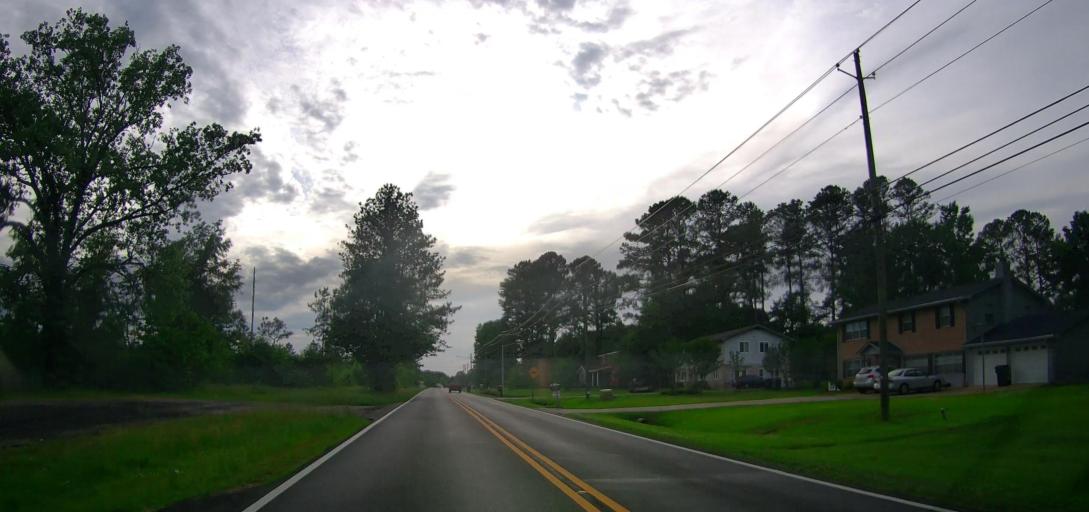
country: US
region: Alabama
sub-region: Calhoun County
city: Oxford
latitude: 33.5856
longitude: -85.7952
